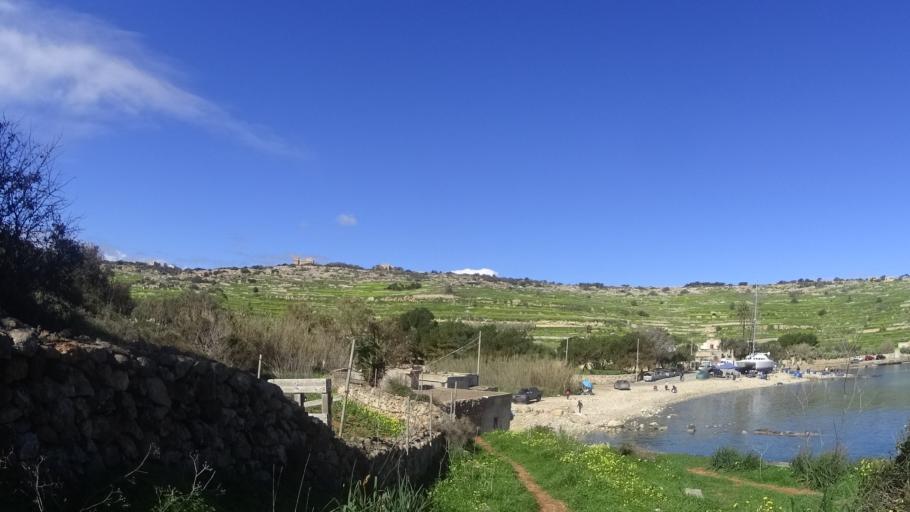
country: MT
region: Saint Paul's Bay
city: San Pawl il-Bahar
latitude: 35.9573
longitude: 14.3903
